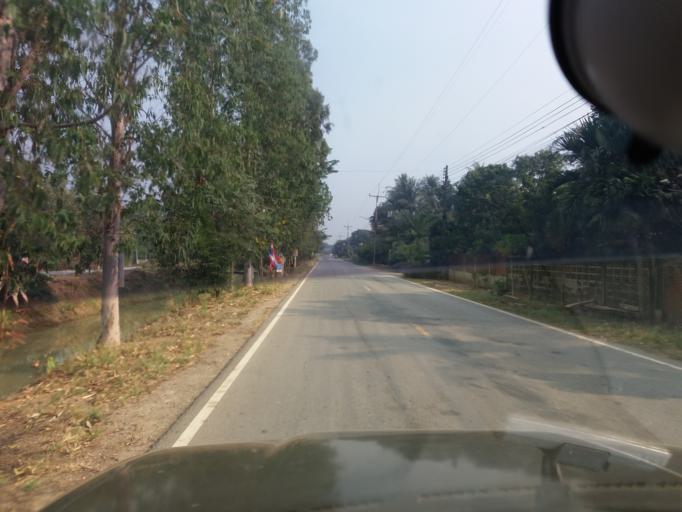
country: TH
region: Suphan Buri
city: Doem Bang Nang Buat
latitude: 14.8998
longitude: 100.1903
